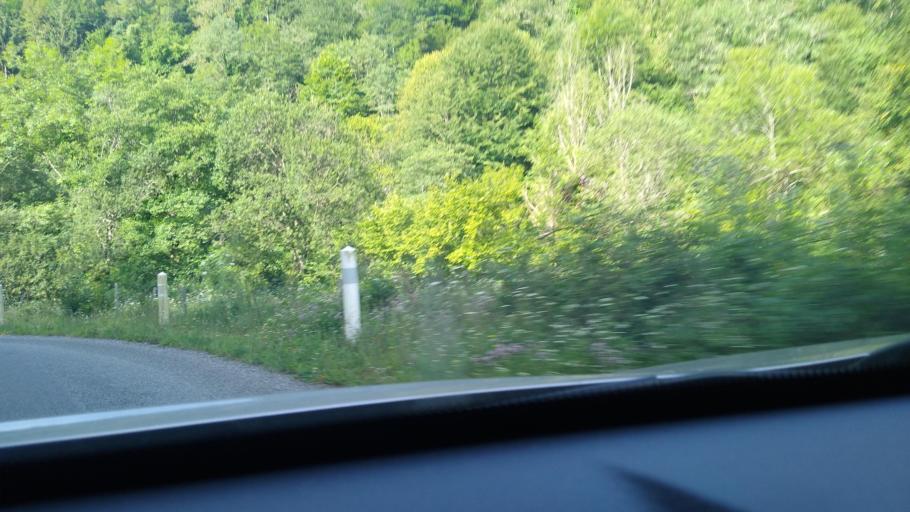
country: FR
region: Midi-Pyrenees
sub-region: Departement de l'Ariege
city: Saint-Girons
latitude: 42.8491
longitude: 1.1916
